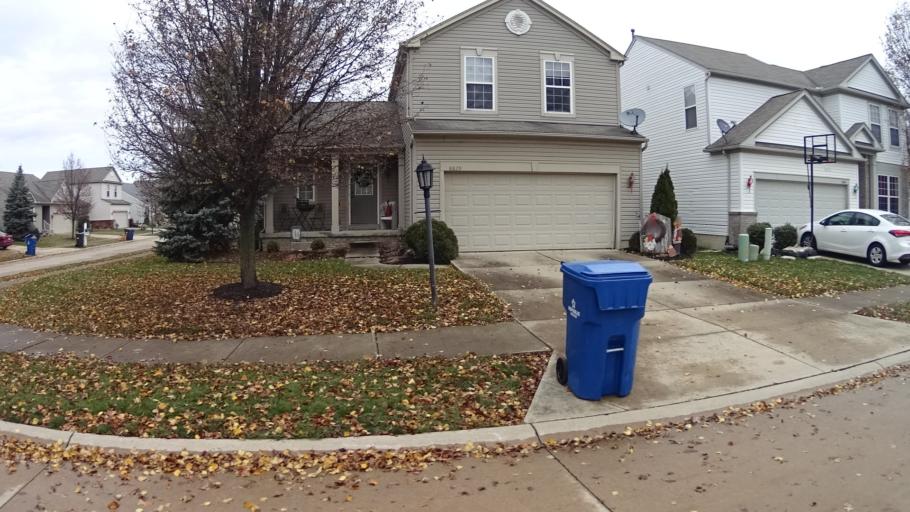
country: US
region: Ohio
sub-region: Lorain County
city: North Ridgeville
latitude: 41.3633
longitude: -82.0442
